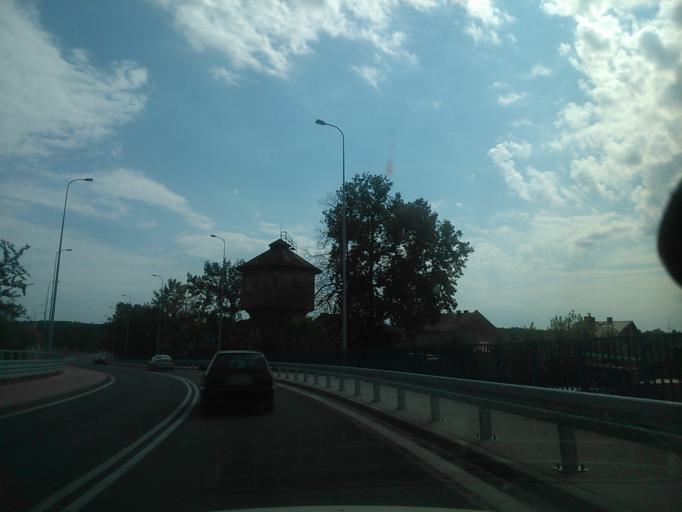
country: PL
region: Warmian-Masurian Voivodeship
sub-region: Powiat dzialdowski
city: Ilowo -Osada
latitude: 53.1654
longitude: 20.2930
